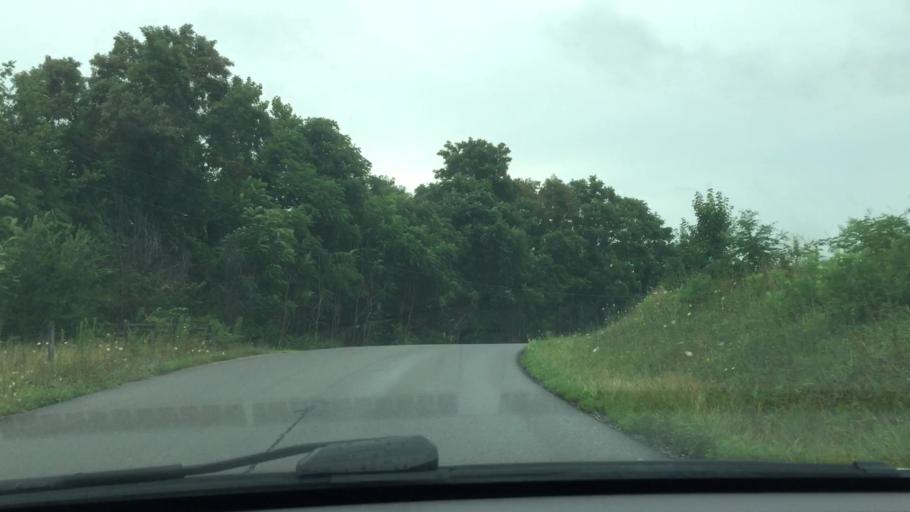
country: US
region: Pennsylvania
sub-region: Washington County
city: Muse
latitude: 40.2958
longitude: -80.1939
